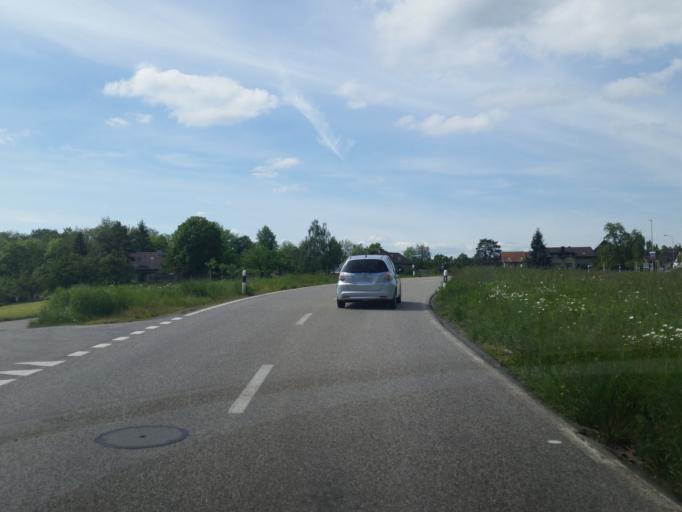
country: CH
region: Aargau
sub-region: Bezirk Bremgarten
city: Unterlunkhofen
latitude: 47.3308
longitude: 8.3859
